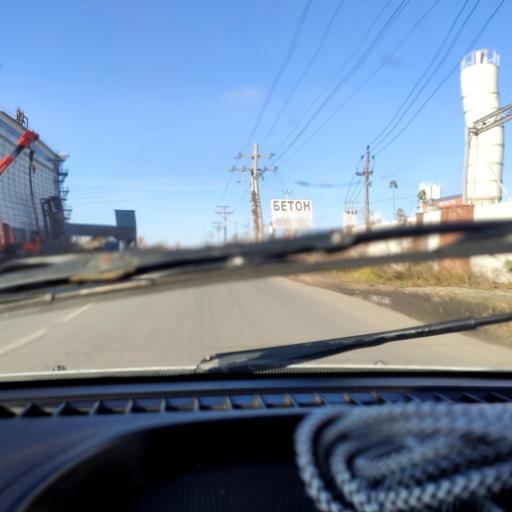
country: RU
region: Samara
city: Zhigulevsk
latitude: 53.5245
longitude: 49.4873
